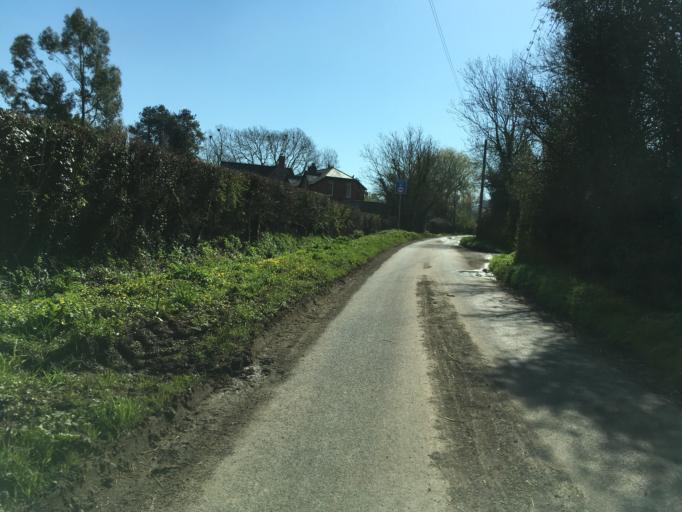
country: GB
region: England
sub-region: Gloucestershire
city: Berkeley
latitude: 51.6853
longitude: -2.4662
